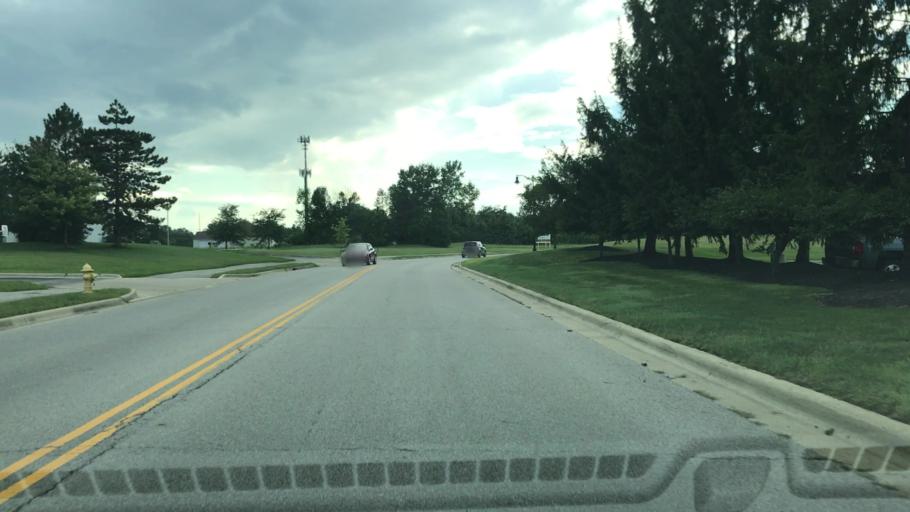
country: US
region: Ohio
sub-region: Franklin County
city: Grove City
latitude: 39.8873
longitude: -83.0641
